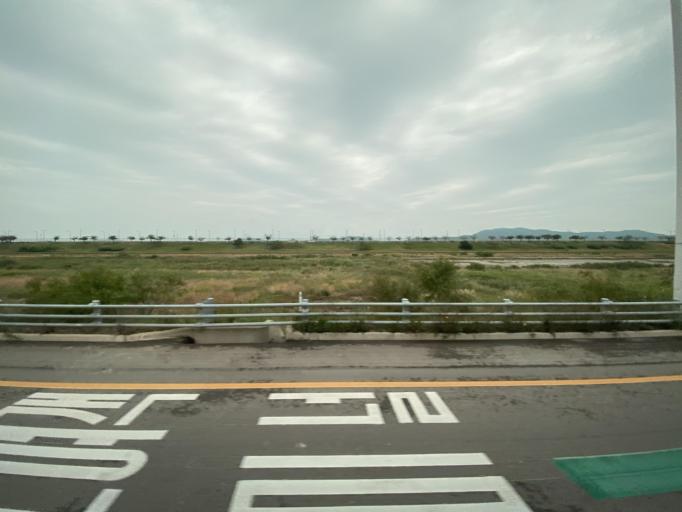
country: KR
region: Incheon
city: Seonwon
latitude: 37.4955
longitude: 126.4258
